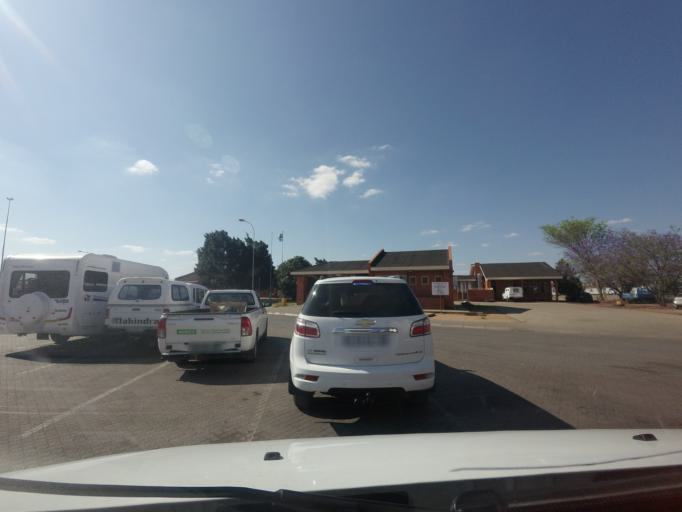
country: BW
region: Central
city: Makobeng
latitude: -22.9966
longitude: 27.9386
